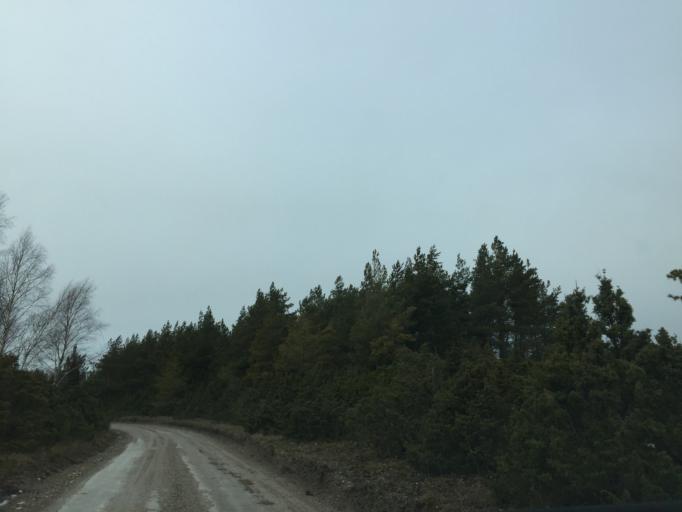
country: EE
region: Saare
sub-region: Kuressaare linn
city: Kuressaare
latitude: 58.4996
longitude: 21.9227
